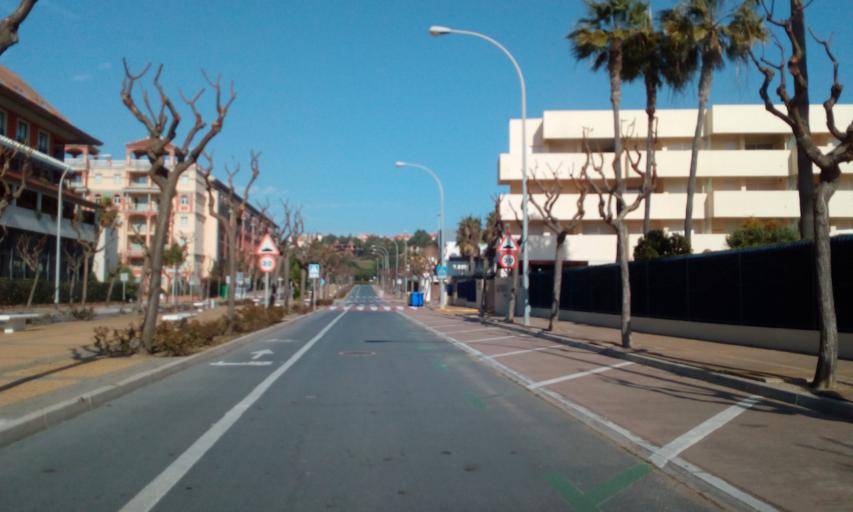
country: ES
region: Andalusia
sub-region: Provincia de Huelva
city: Lepe
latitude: 37.2060
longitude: -7.2295
